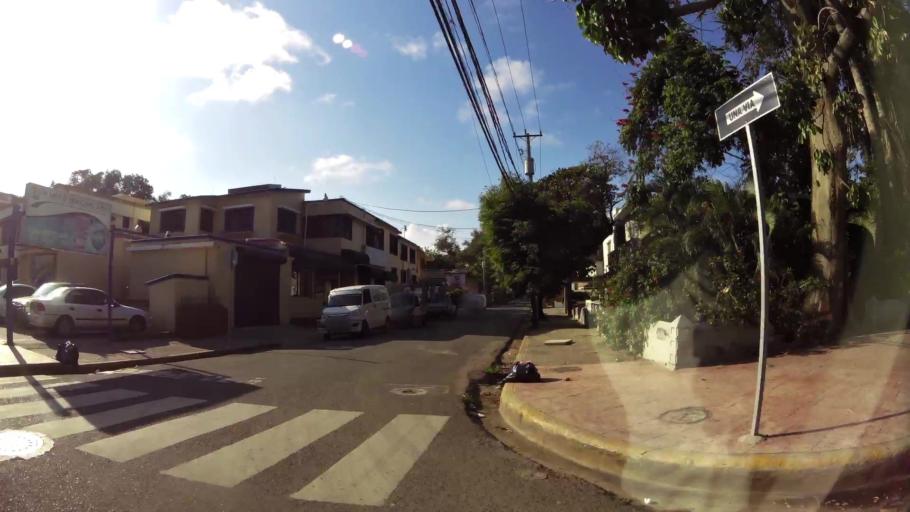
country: DO
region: Nacional
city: Ciudad Nueva
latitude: 18.4578
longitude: -69.9123
